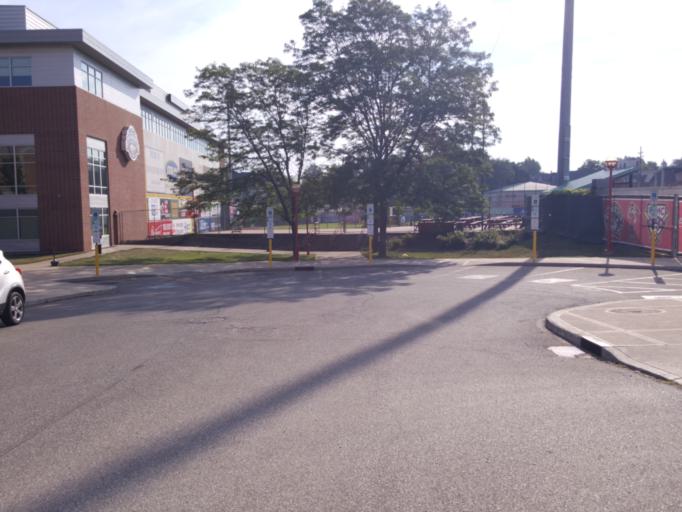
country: US
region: Pennsylvania
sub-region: Erie County
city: Erie
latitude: 42.1272
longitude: -80.0815
